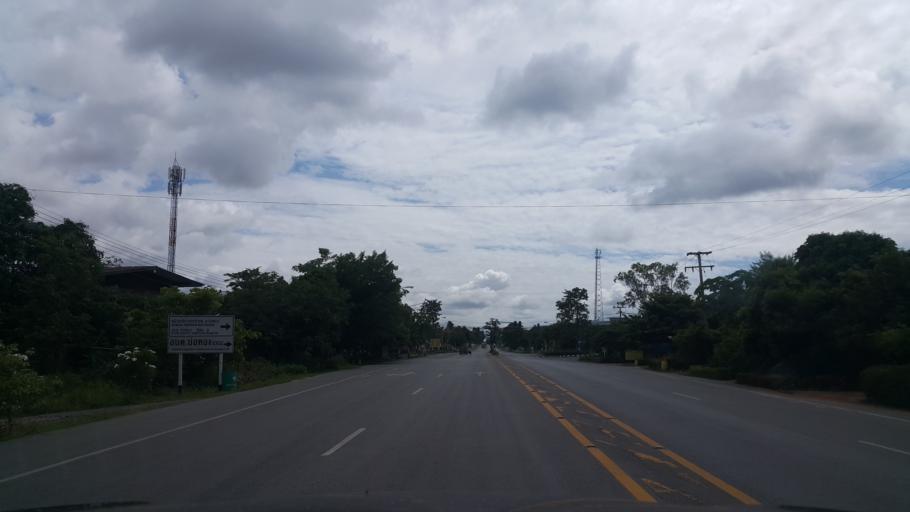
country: TH
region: Uttaradit
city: Thong Saen Khan
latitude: 17.4111
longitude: 100.3247
